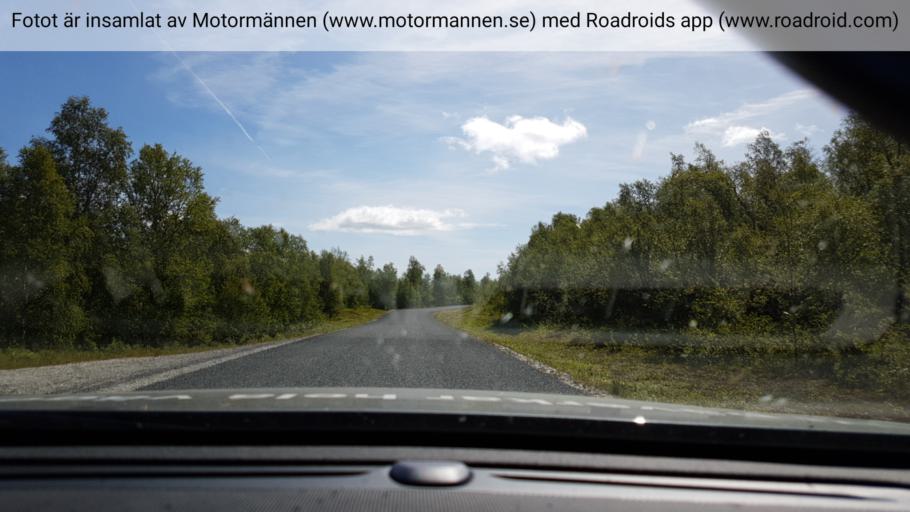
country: NO
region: Nordland
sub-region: Hattfjelldal
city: Hattfjelldal
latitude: 65.4085
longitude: 14.9427
